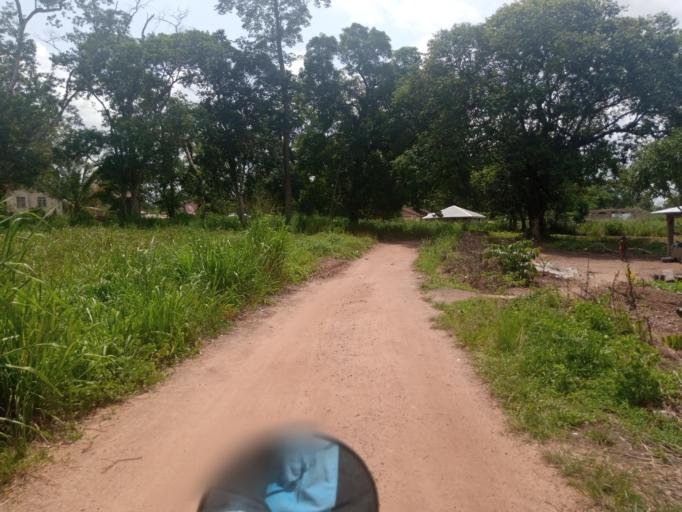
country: SL
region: Southern Province
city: Bo
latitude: 7.9664
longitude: -11.7509
